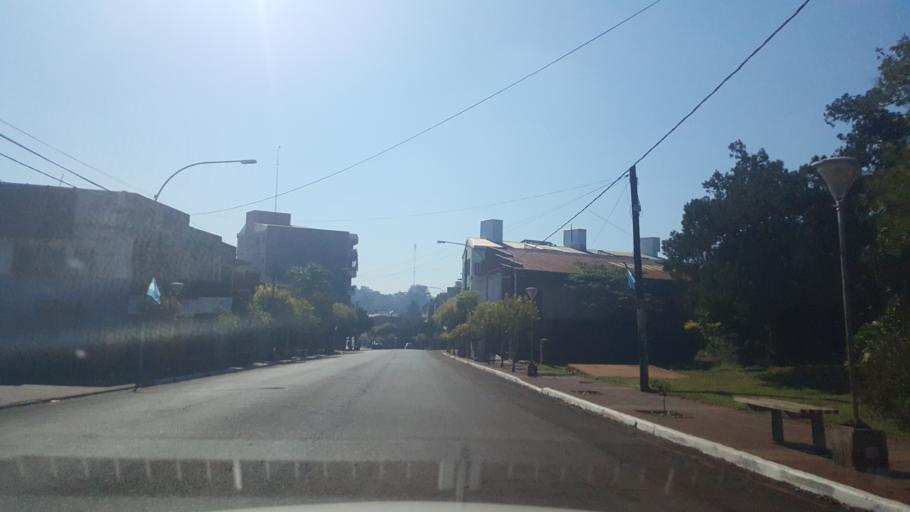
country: AR
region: Misiones
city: Puerto Rico
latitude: -26.8163
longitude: -55.0271
